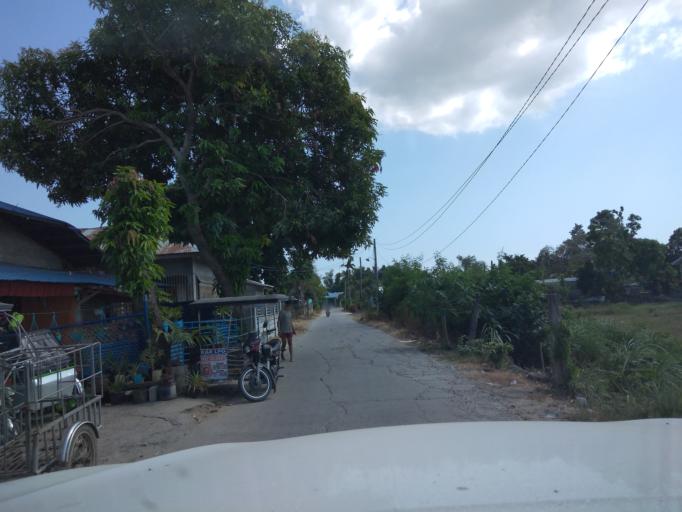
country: PH
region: Central Luzon
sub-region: Province of Pampanga
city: Candaba
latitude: 15.0918
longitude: 120.8147
